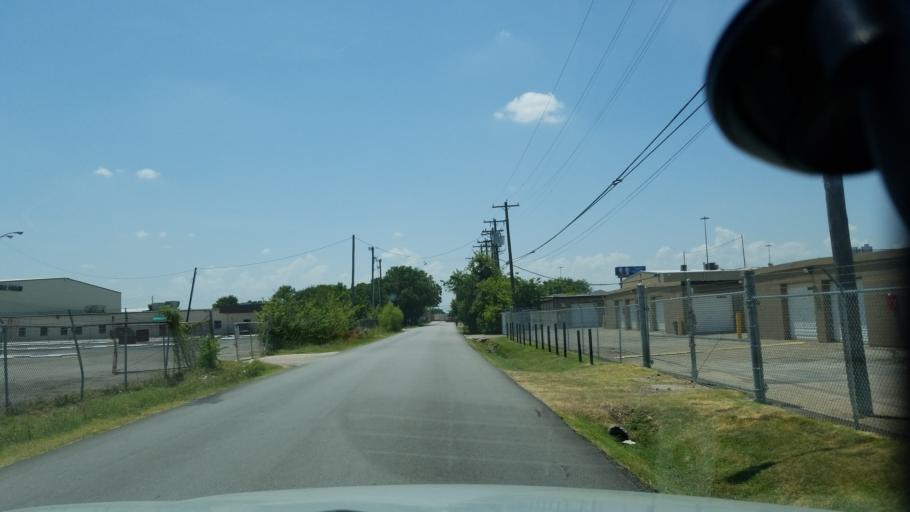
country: US
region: Texas
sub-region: Dallas County
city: Farmers Branch
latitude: 32.8951
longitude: -96.8960
